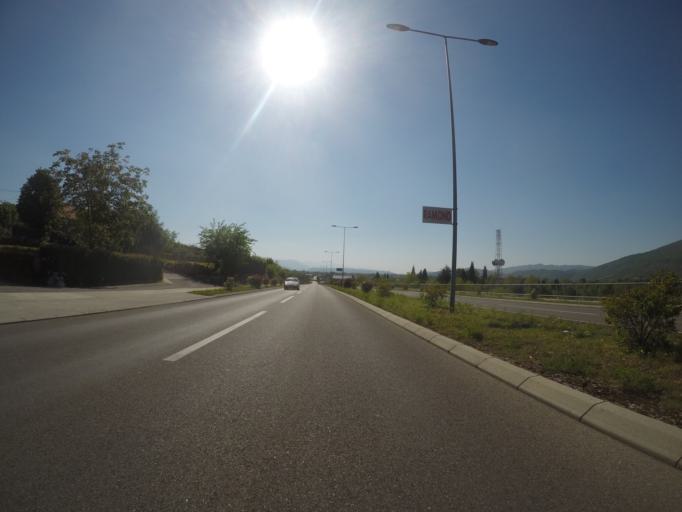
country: ME
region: Danilovgrad
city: Danilovgrad
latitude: 42.5495
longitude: 19.0946
